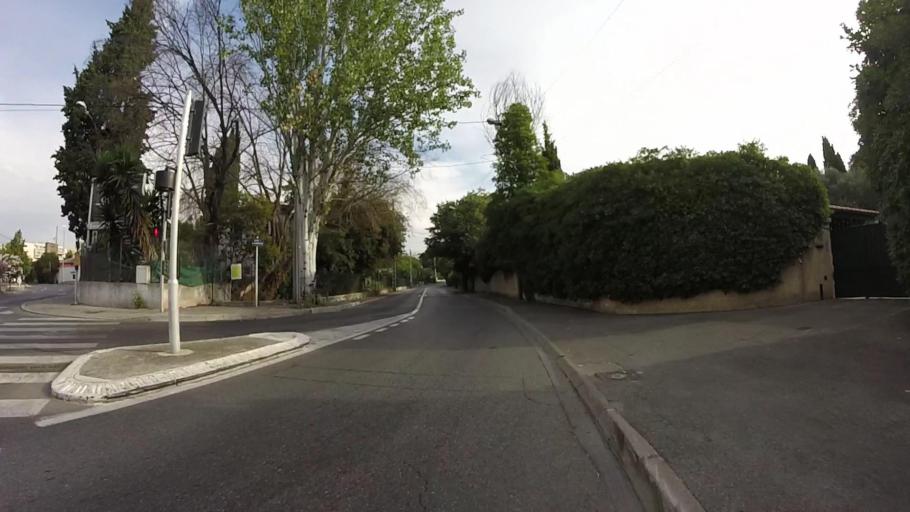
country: FR
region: Provence-Alpes-Cote d'Azur
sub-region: Departement des Alpes-Maritimes
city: Antibes
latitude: 43.5914
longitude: 7.1059
